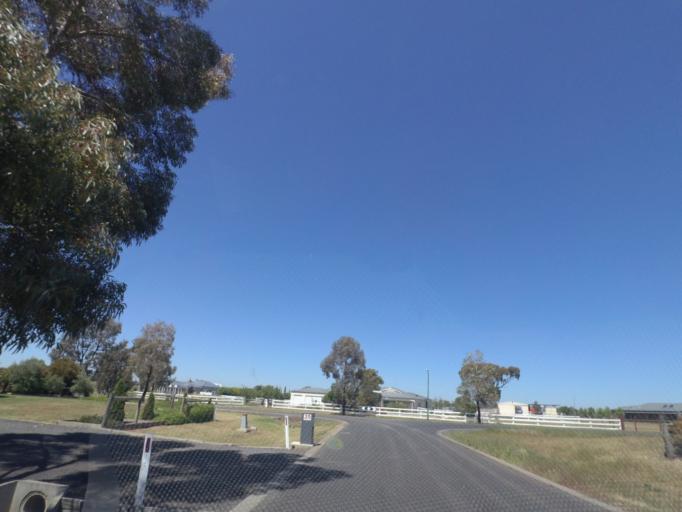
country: AU
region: Victoria
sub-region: Melton
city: Brookfield
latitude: -37.7034
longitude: 144.5078
